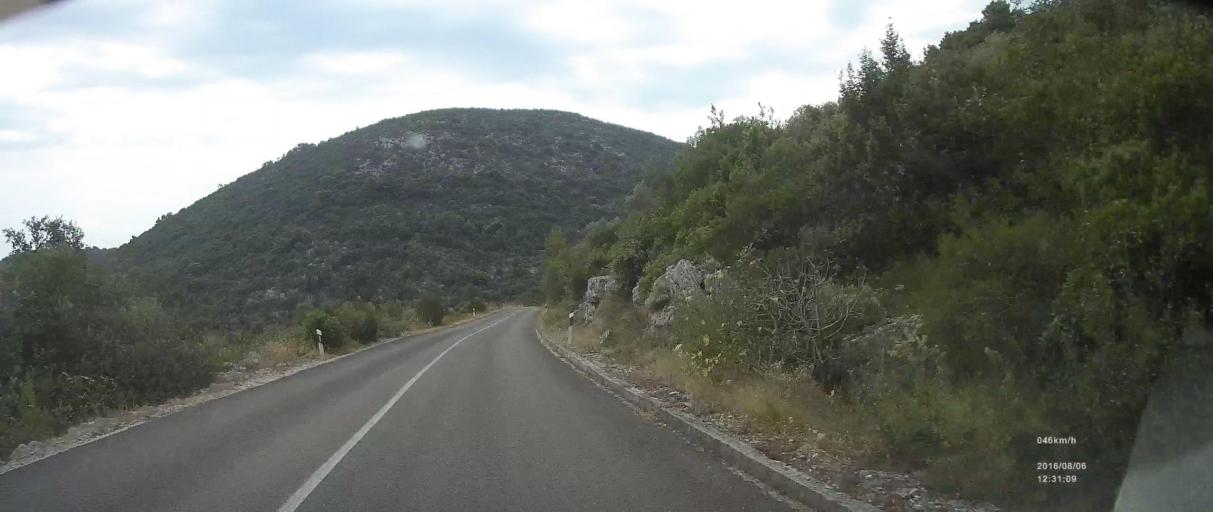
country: HR
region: Dubrovacko-Neretvanska
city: Ston
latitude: 42.7113
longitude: 17.7036
